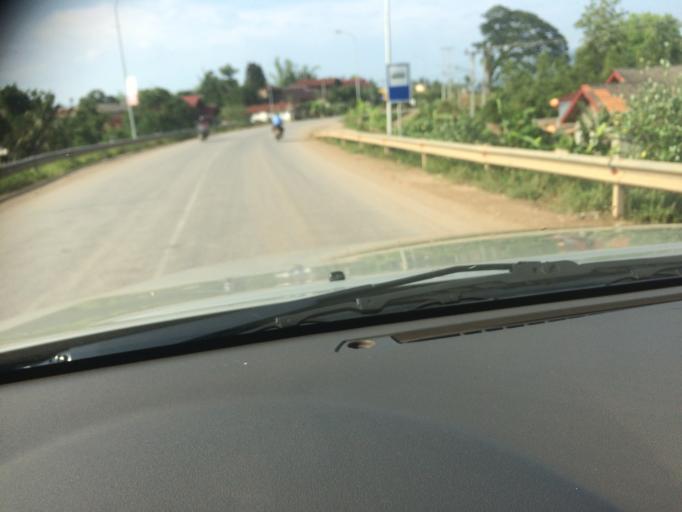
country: LA
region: Xiagnabouli
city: Sainyabuli
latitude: 19.2237
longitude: 101.6906
